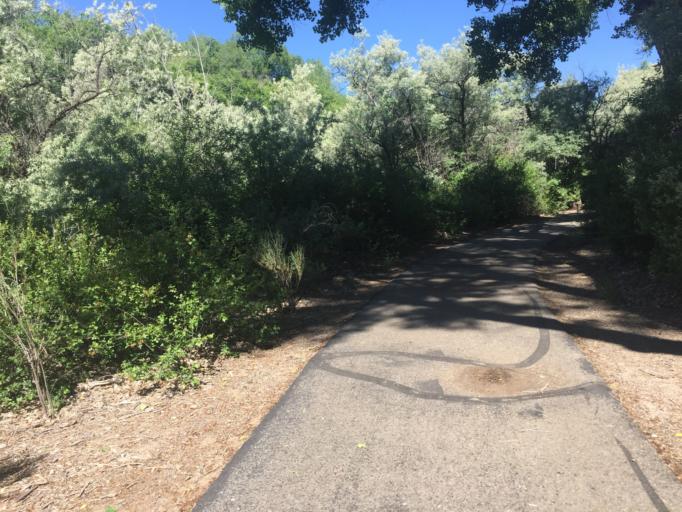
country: US
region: Colorado
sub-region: Mesa County
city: Redlands
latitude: 39.0733
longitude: -108.6038
